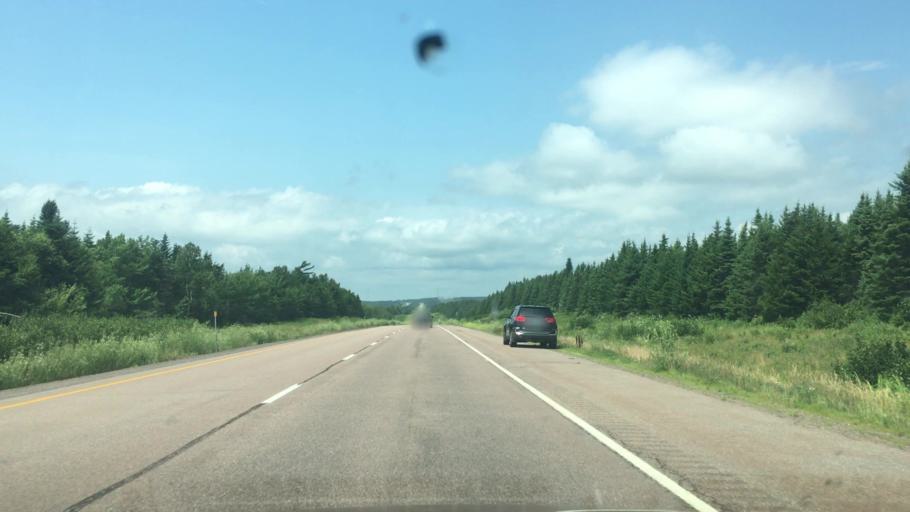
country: CA
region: New Brunswick
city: Sackville
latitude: 45.9712
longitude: -64.4362
